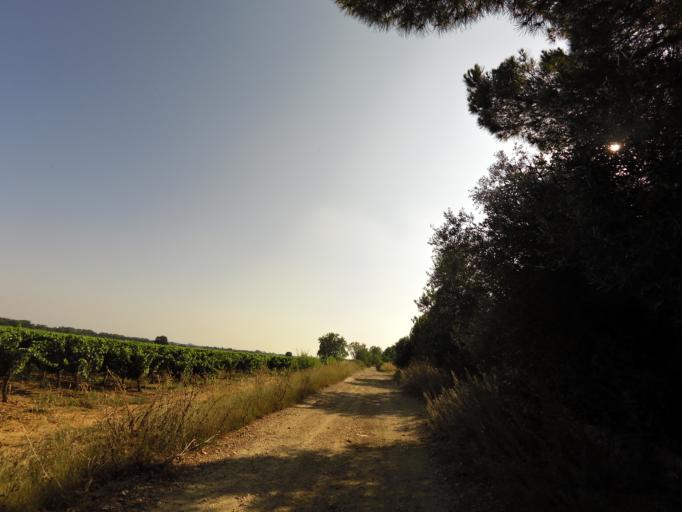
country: FR
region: Languedoc-Roussillon
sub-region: Departement du Gard
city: Mus
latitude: 43.7339
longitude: 4.2086
